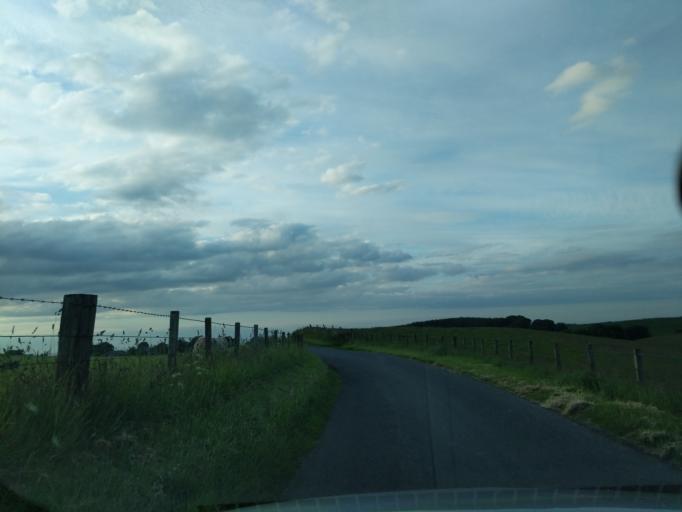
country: GB
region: Scotland
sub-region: Midlothian
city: Gorebridge
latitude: 55.7915
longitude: -3.0923
